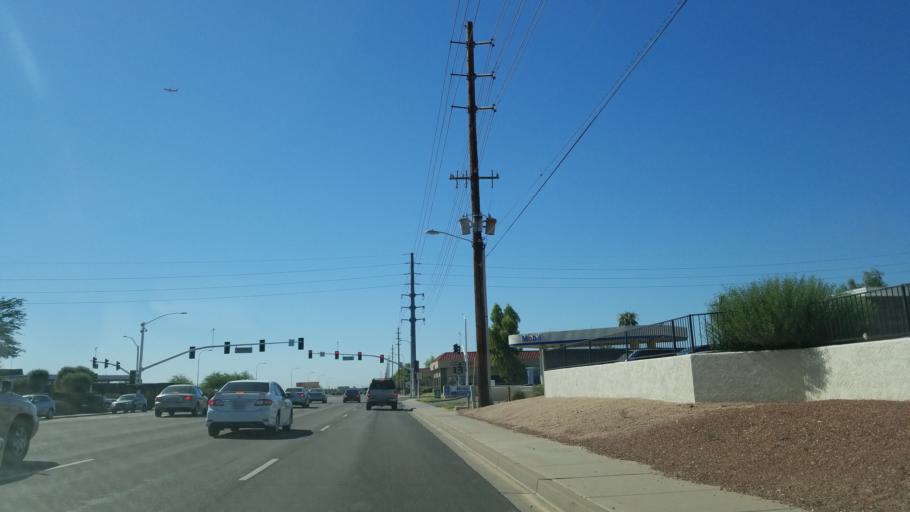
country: US
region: Arizona
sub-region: Maricopa County
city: Tempe
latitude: 33.4523
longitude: -111.9094
